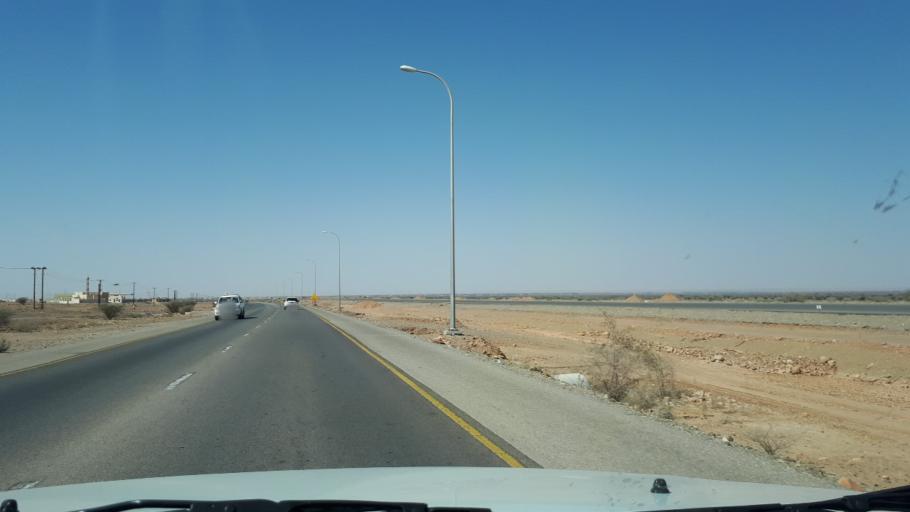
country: OM
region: Ash Sharqiyah
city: Sur
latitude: 22.3087
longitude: 59.2886
